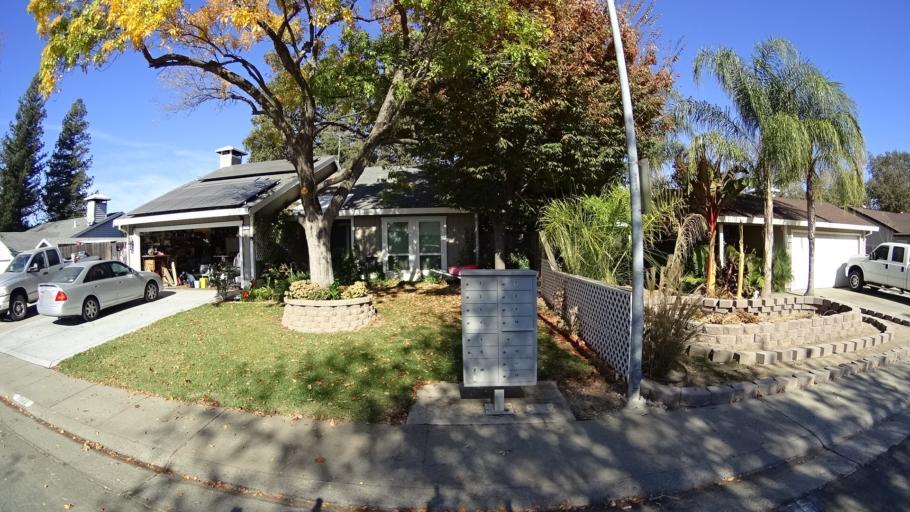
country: US
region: California
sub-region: Sacramento County
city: Citrus Heights
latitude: 38.7187
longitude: -121.3039
